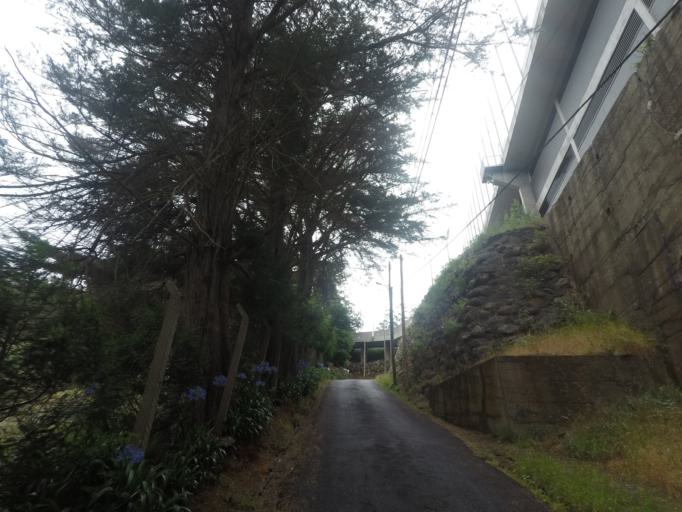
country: PT
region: Madeira
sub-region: Funchal
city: Nossa Senhora do Monte
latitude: 32.6717
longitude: -16.8841
